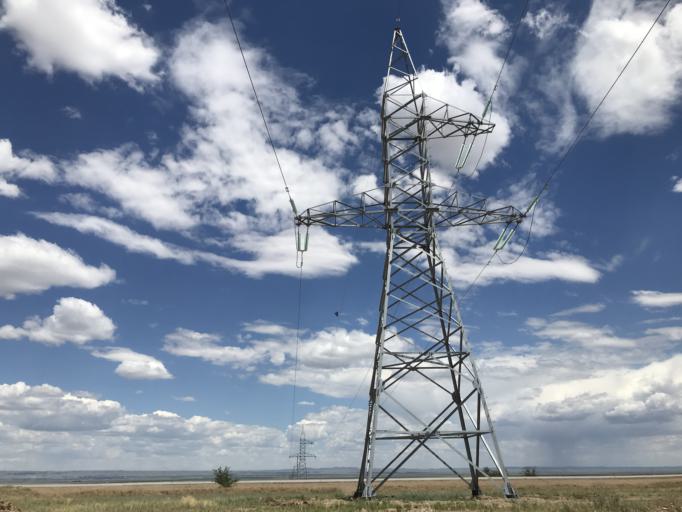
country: KG
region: Chuy
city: Ivanovka
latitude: 43.3743
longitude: 75.2539
